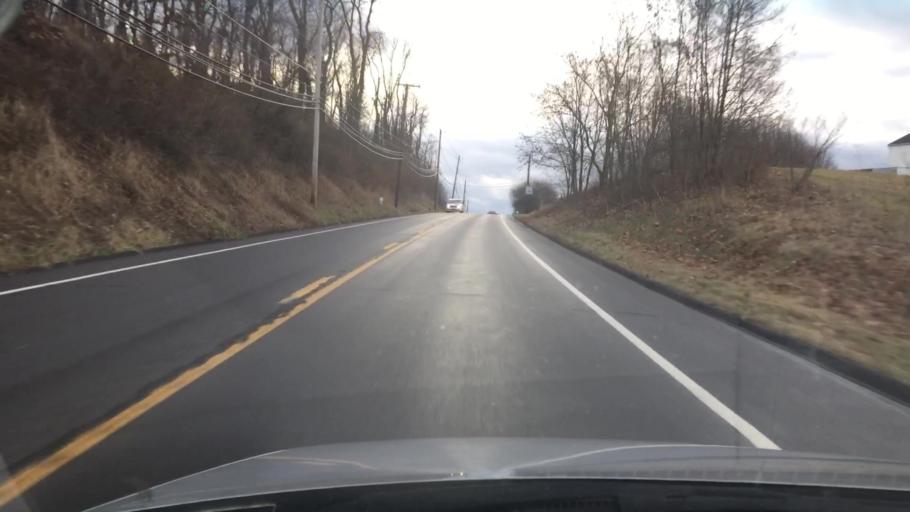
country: US
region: Pennsylvania
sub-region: Columbia County
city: Bloomsburg
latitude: 41.0166
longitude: -76.4687
